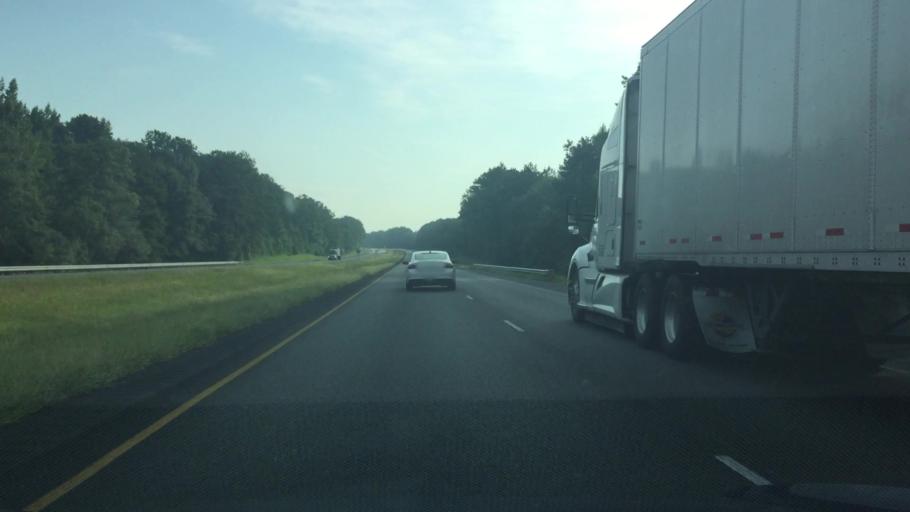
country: US
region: Alabama
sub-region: Butler County
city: Greenville
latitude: 31.7767
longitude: -86.6881
